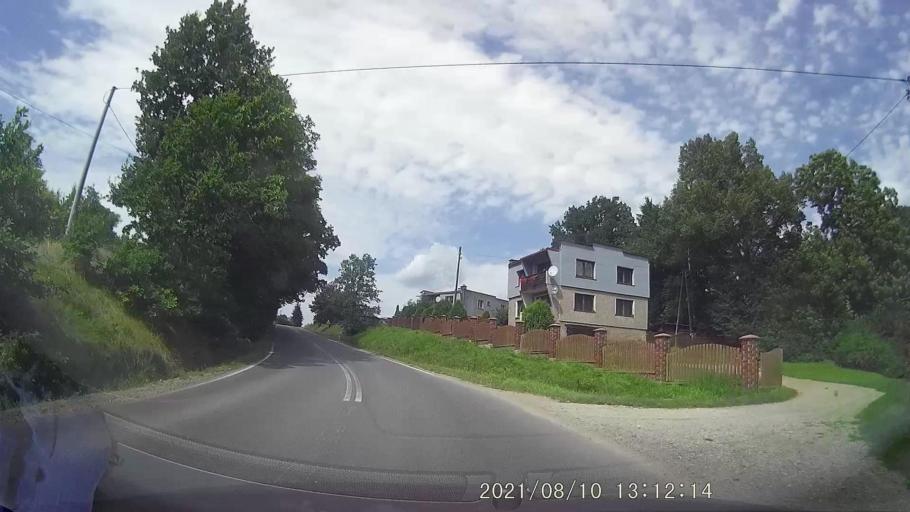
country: PL
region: Lower Silesian Voivodeship
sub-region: Powiat klodzki
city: Bozkow
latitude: 50.5141
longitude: 16.5144
